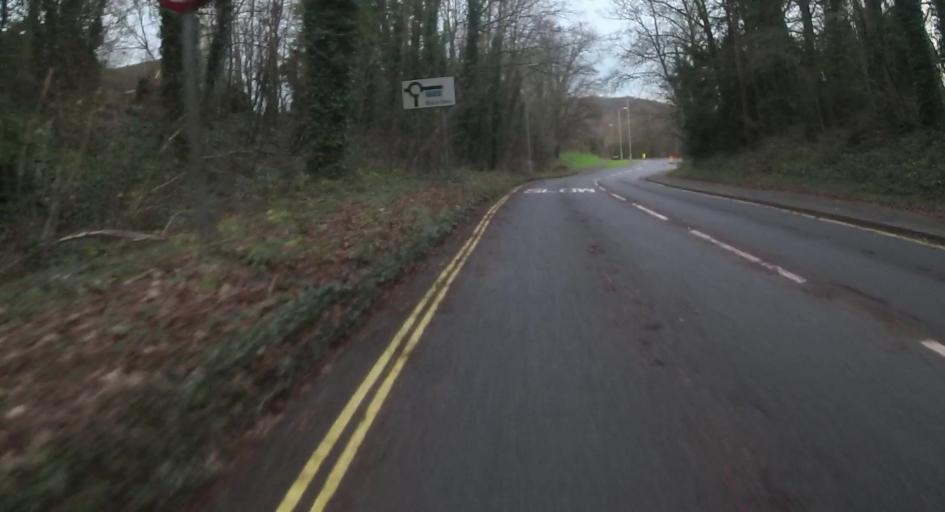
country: GB
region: England
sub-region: Hampshire
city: Basingstoke
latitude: 51.2636
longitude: -1.0709
